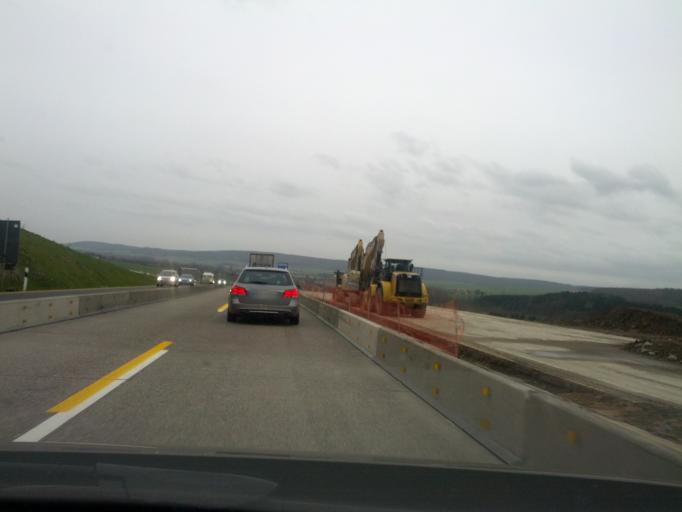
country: DE
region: Lower Saxony
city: Bockenem
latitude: 51.9669
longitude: 10.1430
